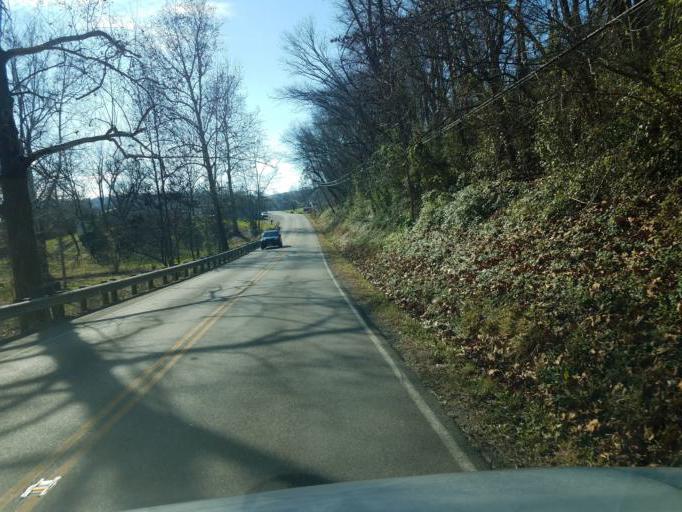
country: US
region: Ohio
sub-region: Scioto County
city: Sciotodale
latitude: 38.7769
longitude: -82.8596
